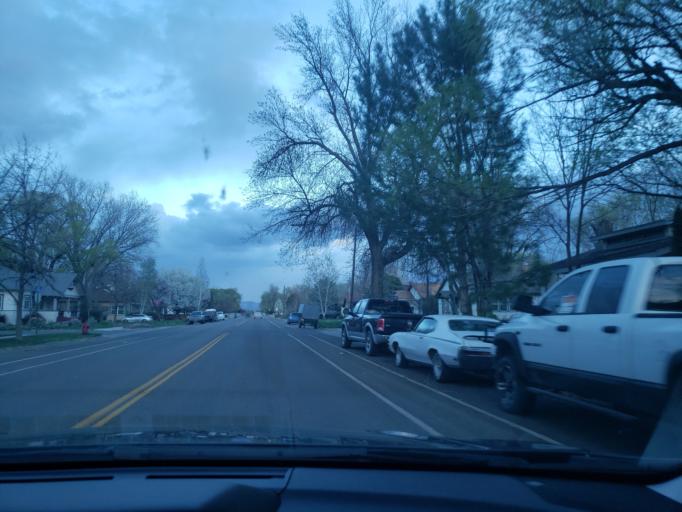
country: US
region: Colorado
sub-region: Mesa County
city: Fruita
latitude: 39.1589
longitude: -108.7260
